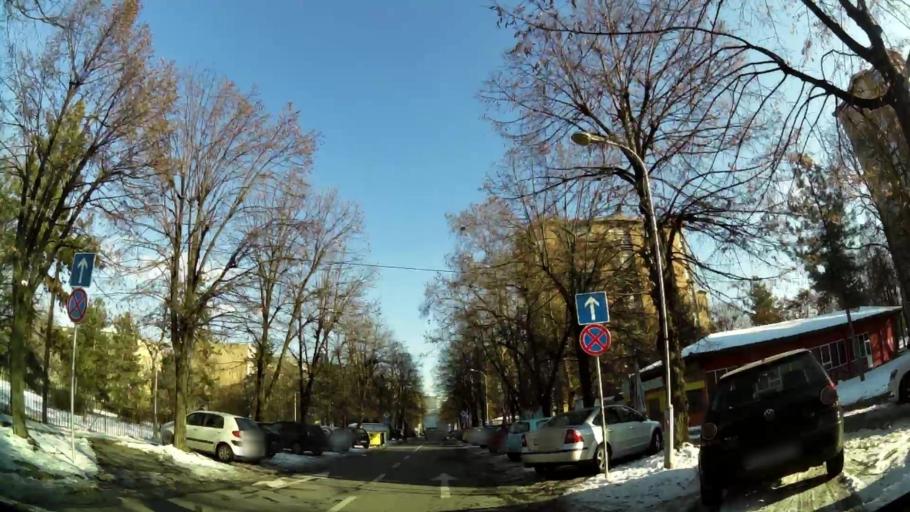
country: MK
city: Krushopek
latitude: 42.0055
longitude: 21.3879
